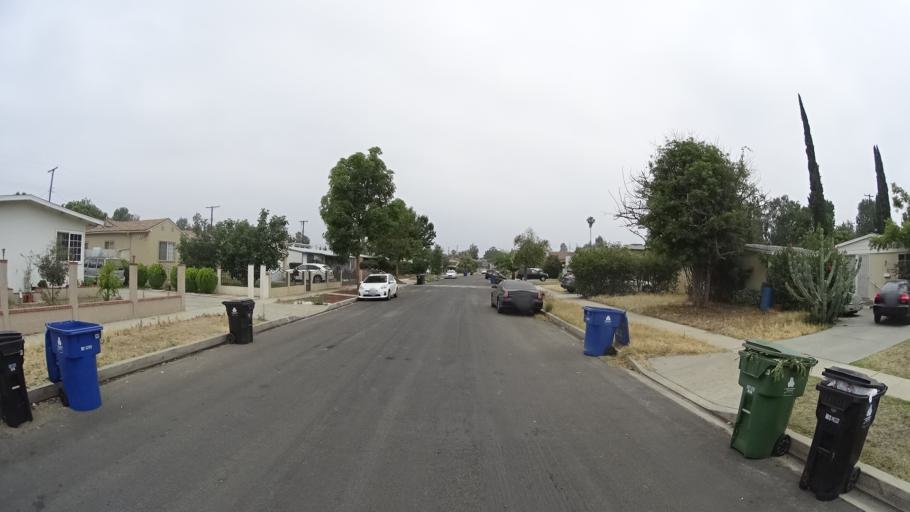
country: US
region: California
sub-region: Los Angeles County
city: Van Nuys
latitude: 34.1911
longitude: -118.4177
